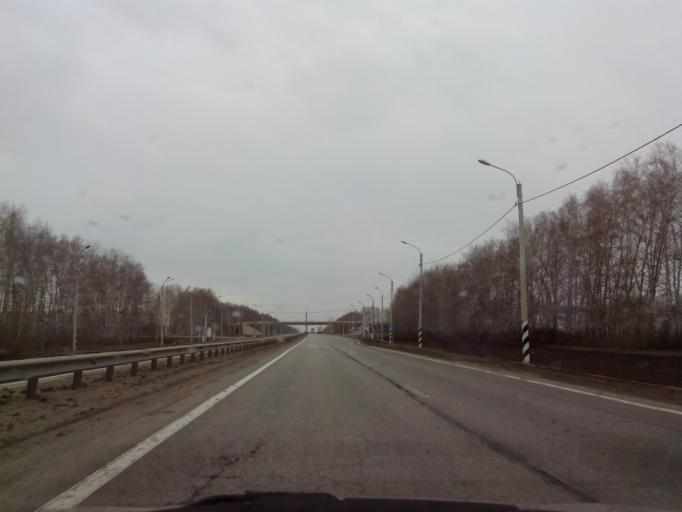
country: RU
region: Tambov
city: Selezni
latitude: 52.7590
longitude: 41.1410
